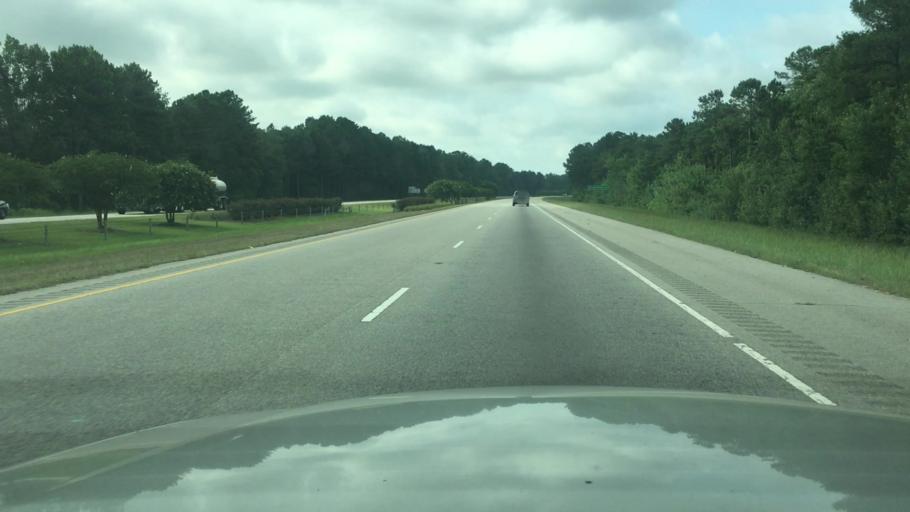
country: US
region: North Carolina
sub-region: Cumberland County
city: Fayetteville
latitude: 34.9998
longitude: -78.8647
